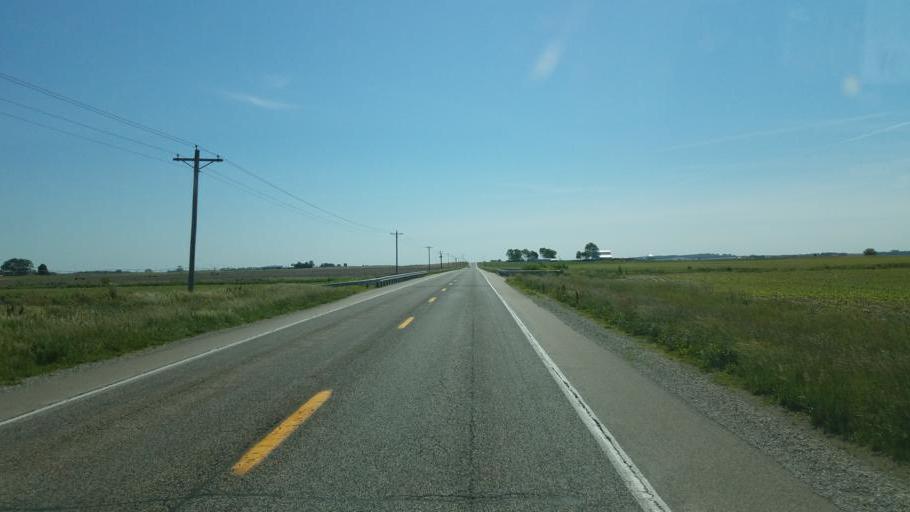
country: US
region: Illinois
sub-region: Mason County
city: Mason City
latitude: 40.3038
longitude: -89.7634
